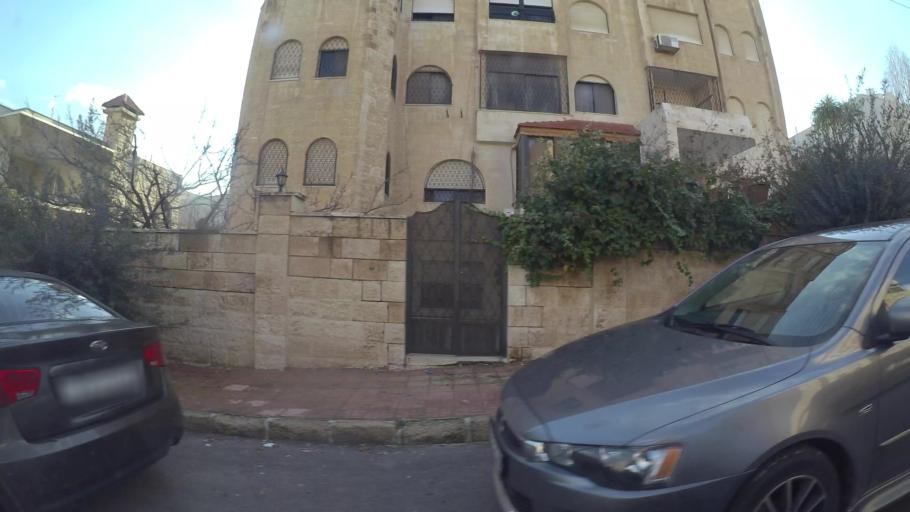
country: JO
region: Amman
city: Al Jubayhah
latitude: 32.0011
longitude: 35.8705
